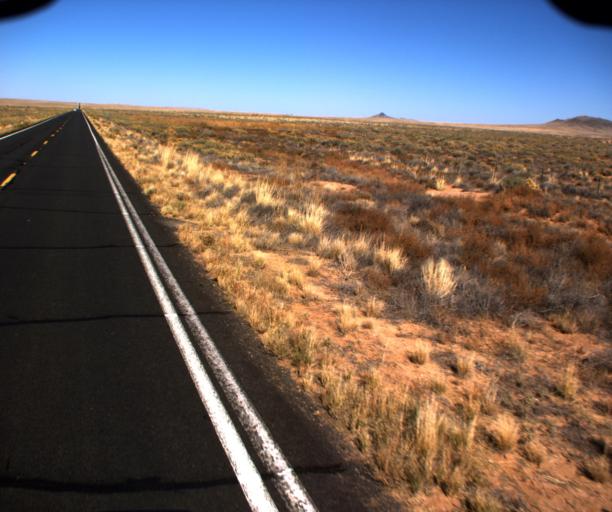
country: US
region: Arizona
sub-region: Navajo County
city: Dilkon
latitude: 35.5692
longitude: -110.4596
